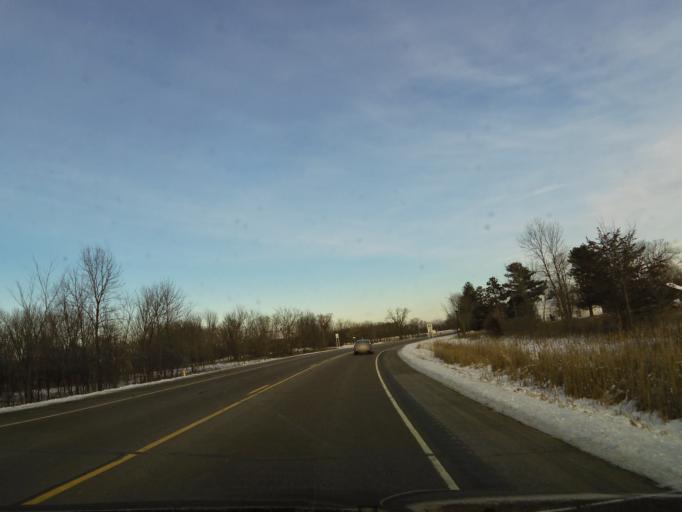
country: US
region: Wisconsin
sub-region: Polk County
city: Osceola
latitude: 45.3095
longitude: -92.7581
